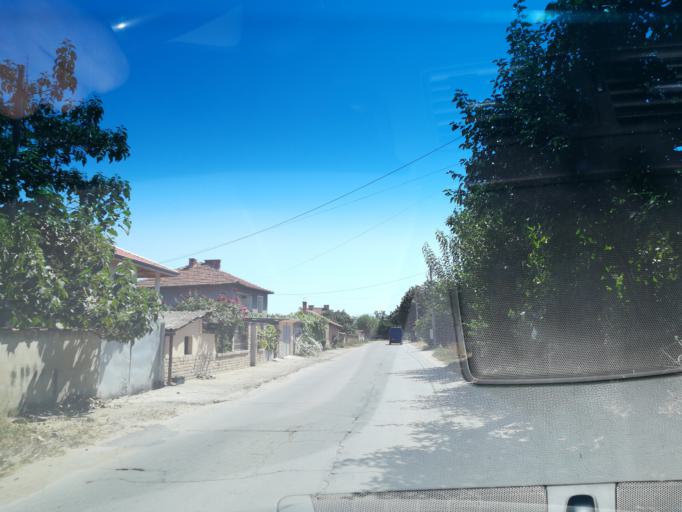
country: BG
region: Pazardzhik
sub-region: Obshtina Pazardzhik
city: Pazardzhik
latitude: 42.2771
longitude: 24.3958
